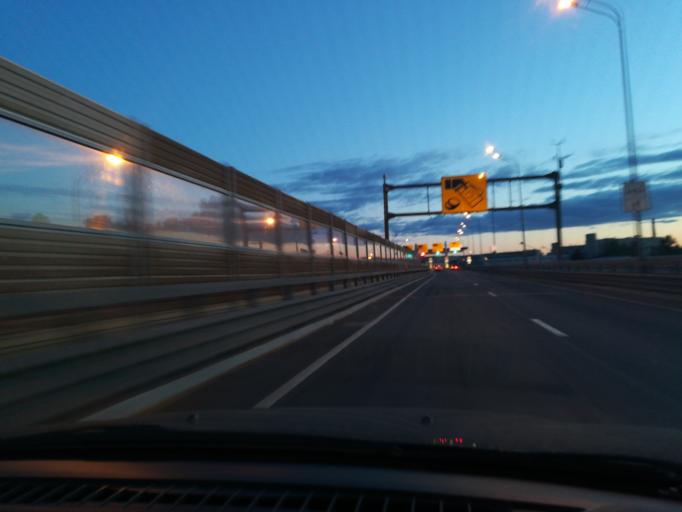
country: RU
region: St.-Petersburg
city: Avtovo
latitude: 59.8555
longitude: 30.2790
